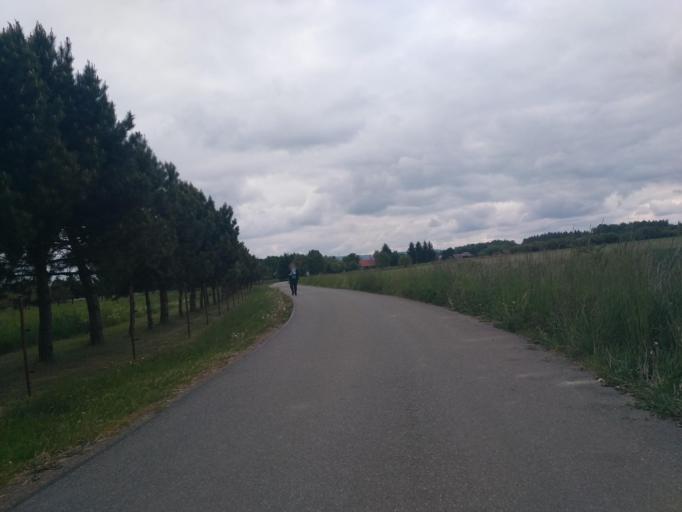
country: PL
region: Subcarpathian Voivodeship
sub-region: Powiat krosnienski
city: Jedlicze
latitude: 49.7080
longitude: 21.6774
